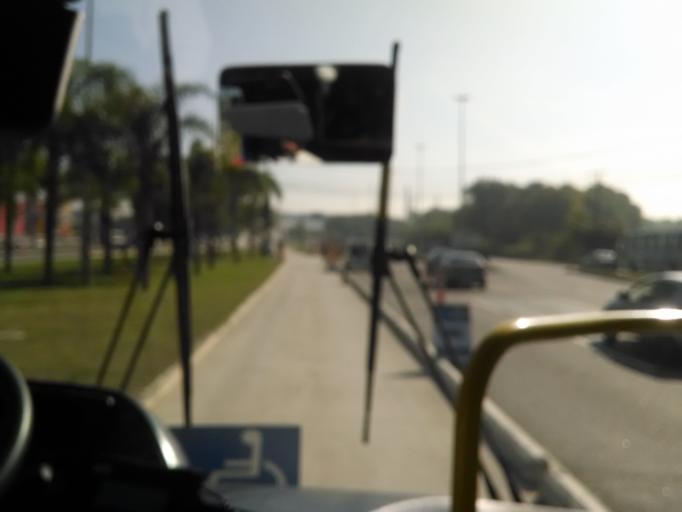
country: BR
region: Rio de Janeiro
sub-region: Rio De Janeiro
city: Rio de Janeiro
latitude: -22.9820
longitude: -43.3655
